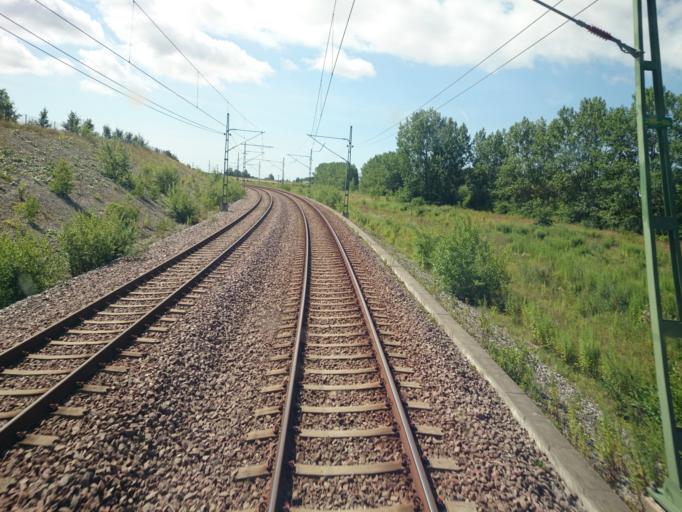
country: SE
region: Skane
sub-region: Malmo
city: Bunkeflostrand
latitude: 55.5549
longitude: 12.9553
